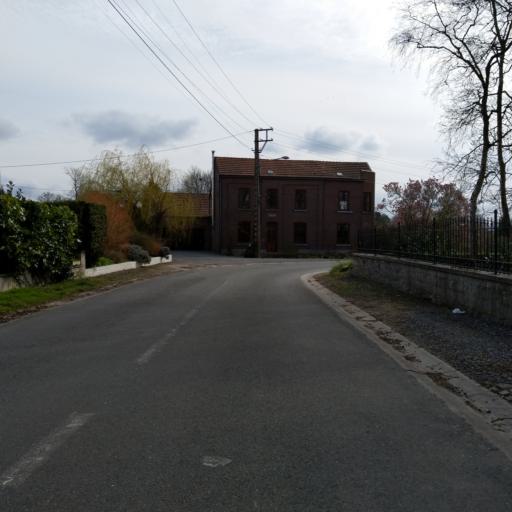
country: BE
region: Wallonia
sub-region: Province du Hainaut
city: Soignies
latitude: 50.5635
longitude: 4.0650
